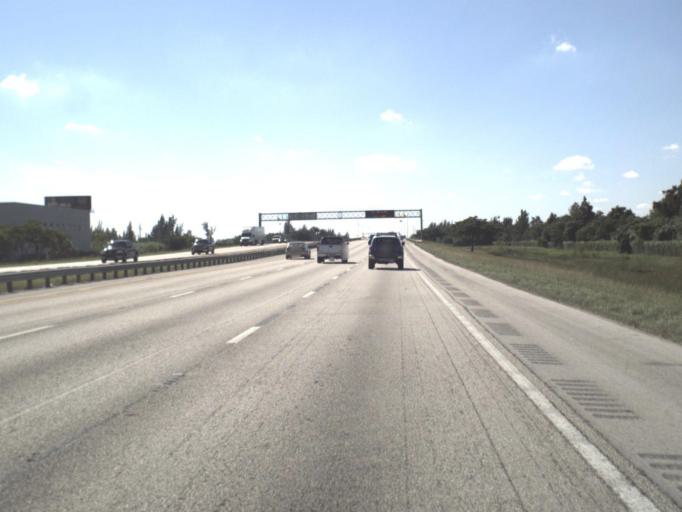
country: US
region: Florida
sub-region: Miami-Dade County
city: Hialeah Gardens
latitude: 25.8872
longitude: -80.3889
